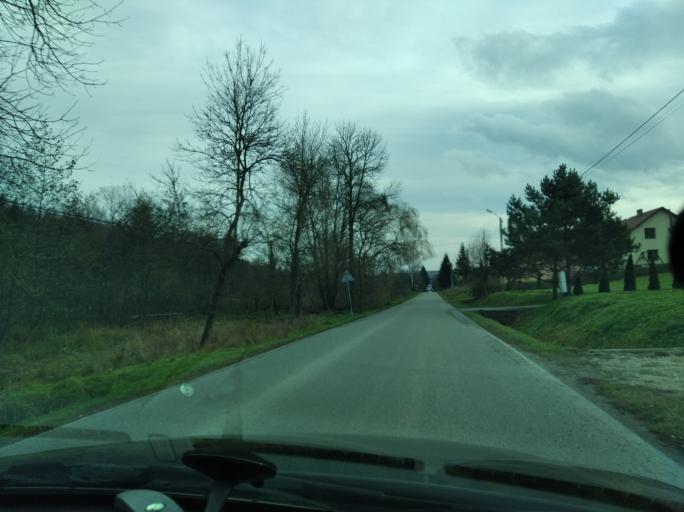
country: PL
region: Subcarpathian Voivodeship
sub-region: Powiat strzyzowski
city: Strzyzow
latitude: 49.9416
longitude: 21.7533
